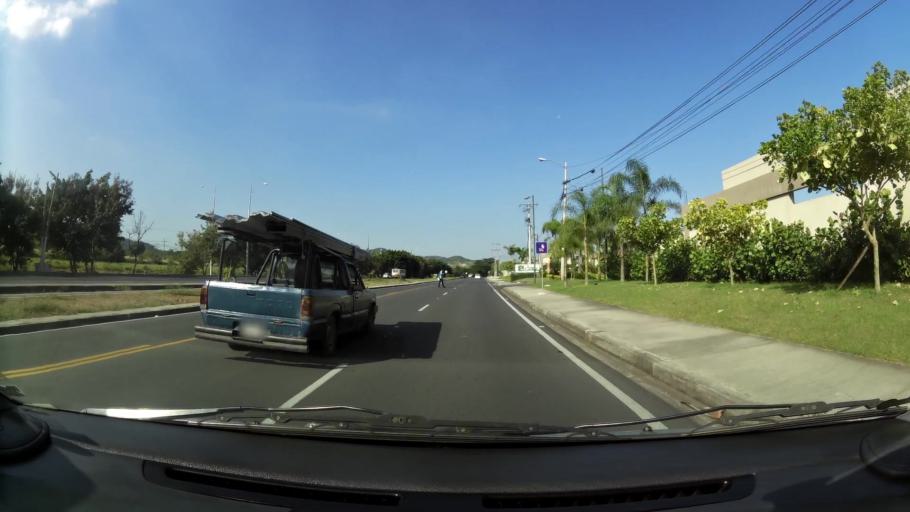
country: EC
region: Guayas
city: Santa Lucia
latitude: -2.1831
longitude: -79.9948
